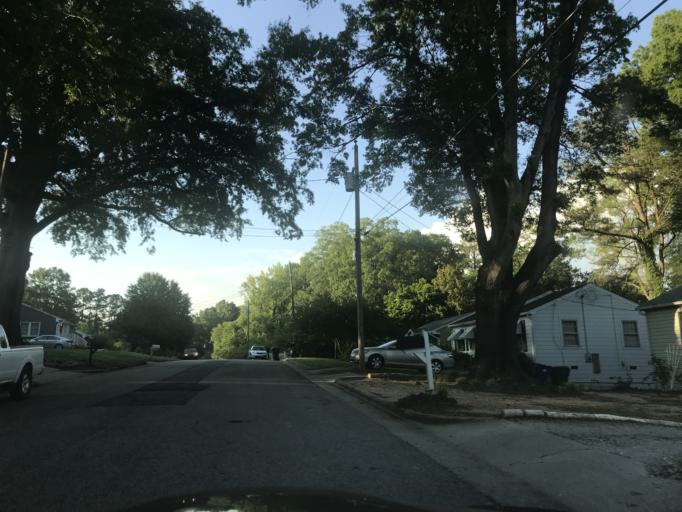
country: US
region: North Carolina
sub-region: Wake County
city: Raleigh
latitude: 35.7452
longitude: -78.6425
